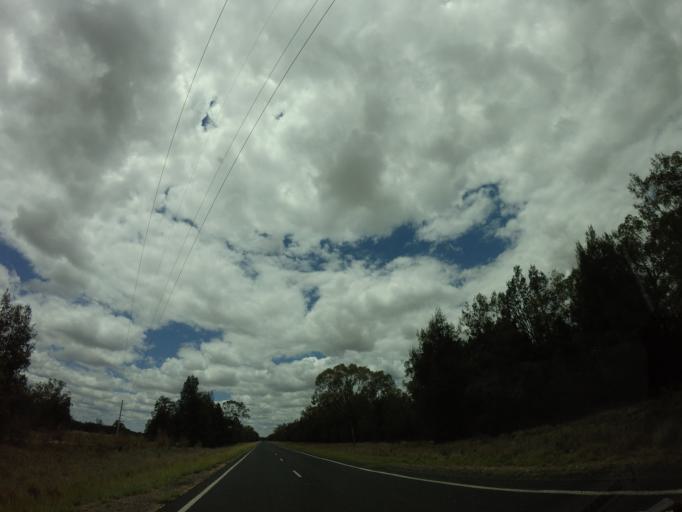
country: AU
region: Queensland
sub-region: Goondiwindi
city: Goondiwindi
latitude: -28.1628
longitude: 150.6190
